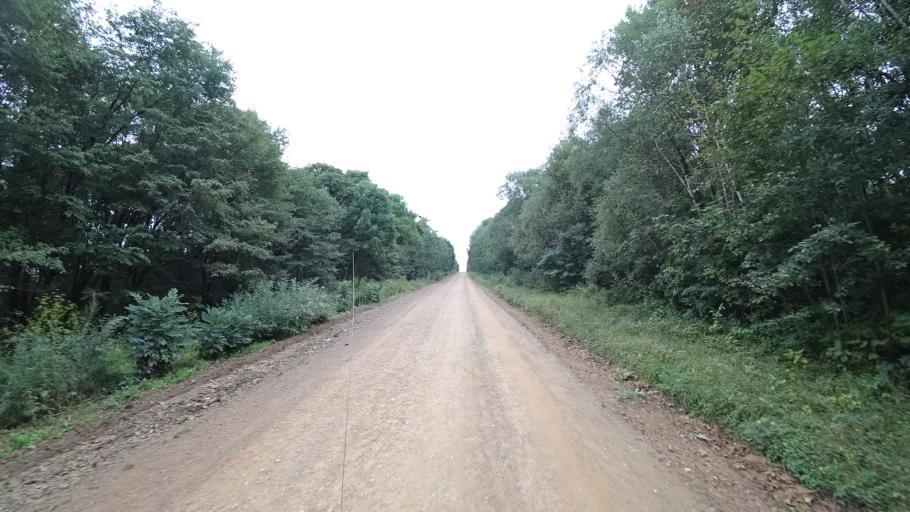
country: RU
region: Primorskiy
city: Rettikhovka
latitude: 44.1716
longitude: 132.8808
